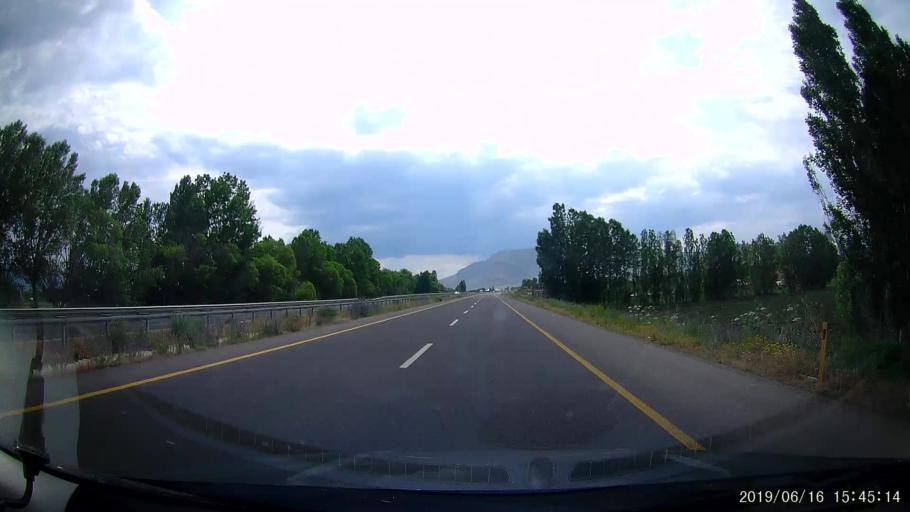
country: TR
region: Erzurum
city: Koprukoy
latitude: 39.9881
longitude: 41.7712
